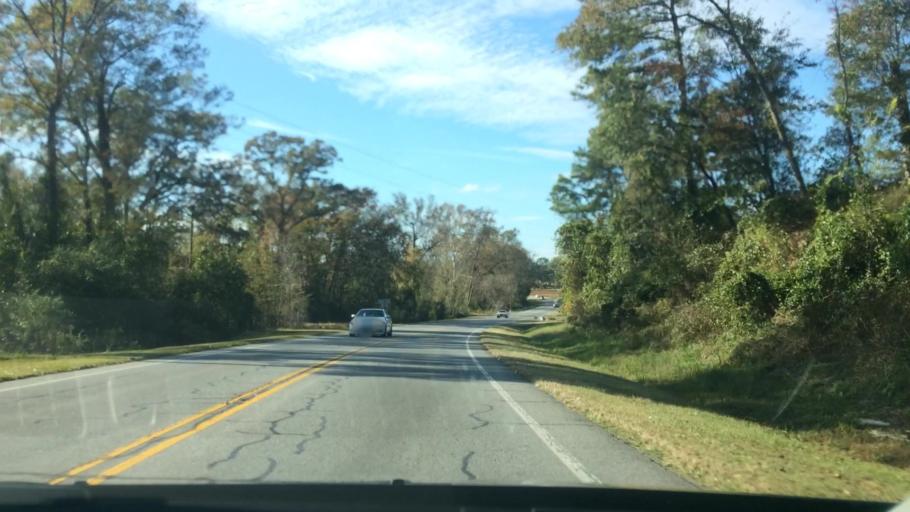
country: US
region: North Carolina
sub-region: Greene County
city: Snow Hill
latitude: 35.4568
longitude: -77.6963
